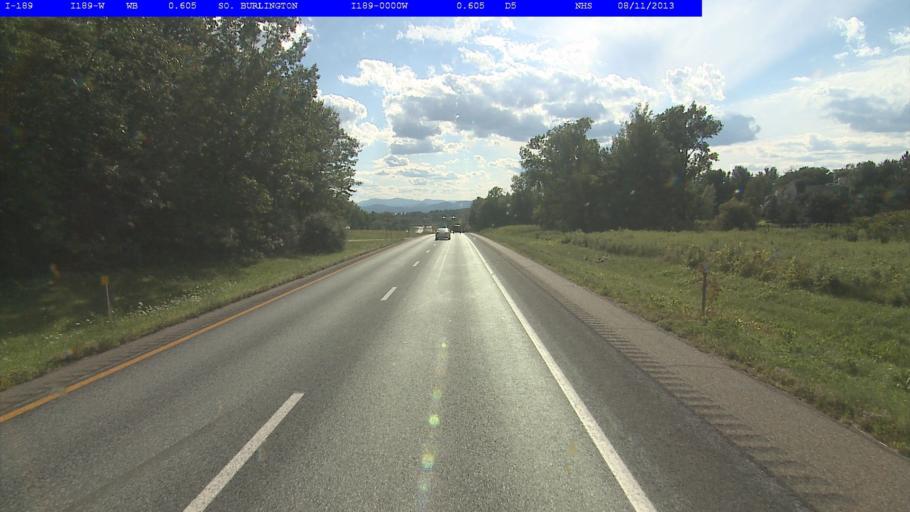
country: US
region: Vermont
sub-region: Chittenden County
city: Burlington
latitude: 44.4498
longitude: -73.1985
